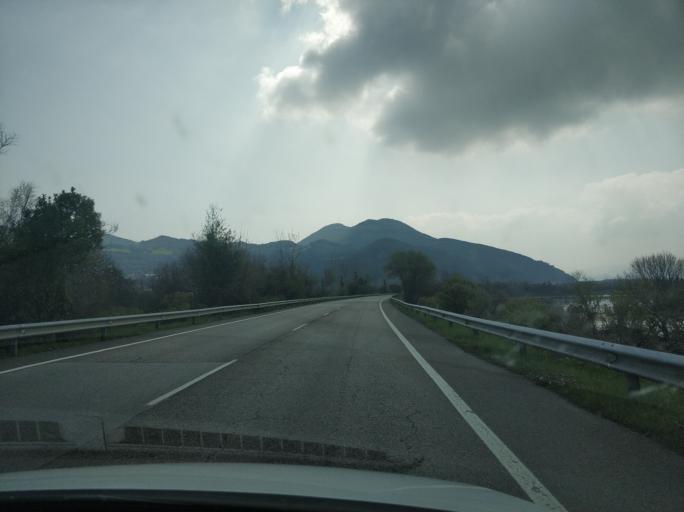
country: ES
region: Cantabria
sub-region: Provincia de Cantabria
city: Santona
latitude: 43.4600
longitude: -3.4689
